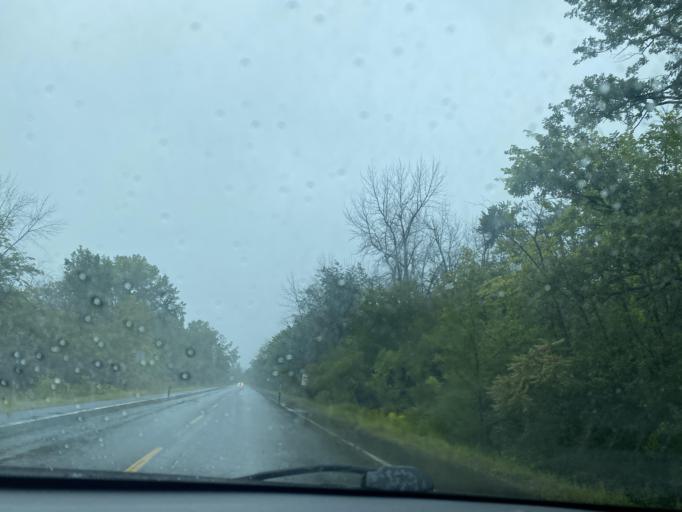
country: CA
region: Quebec
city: Baie-D'Urfe
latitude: 45.4403
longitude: -73.9098
